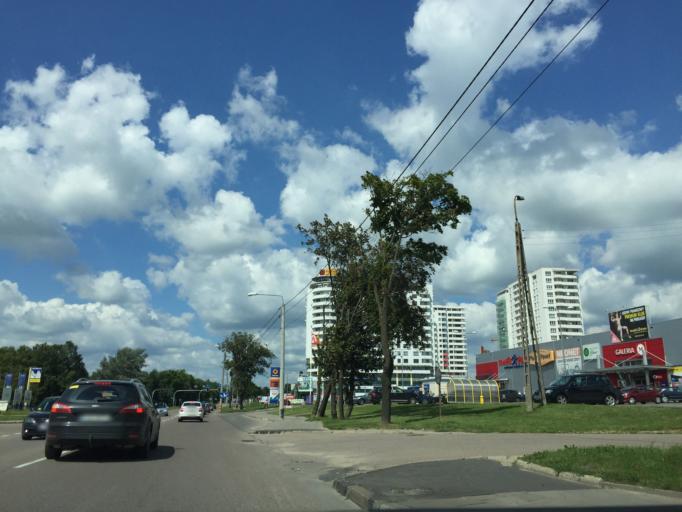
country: PL
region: Podlasie
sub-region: Bialystok
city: Bialystok
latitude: 53.1490
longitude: 23.1561
